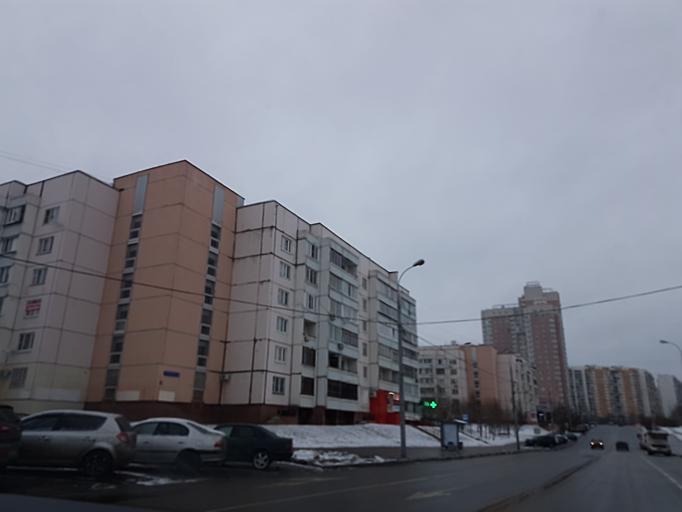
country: RU
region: Moskovskaya
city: Pavshino
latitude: 55.8280
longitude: 37.3536
